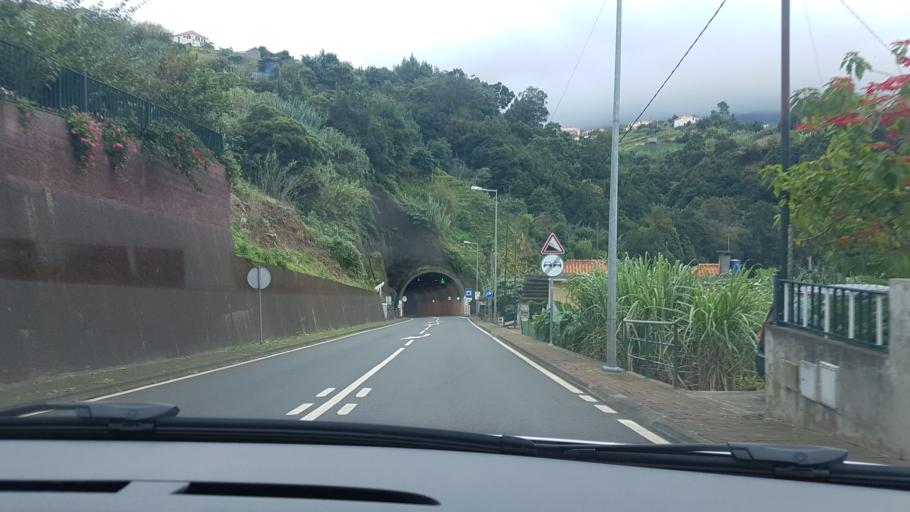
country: PT
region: Madeira
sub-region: Santana
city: Santana
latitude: 32.8195
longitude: -16.8911
